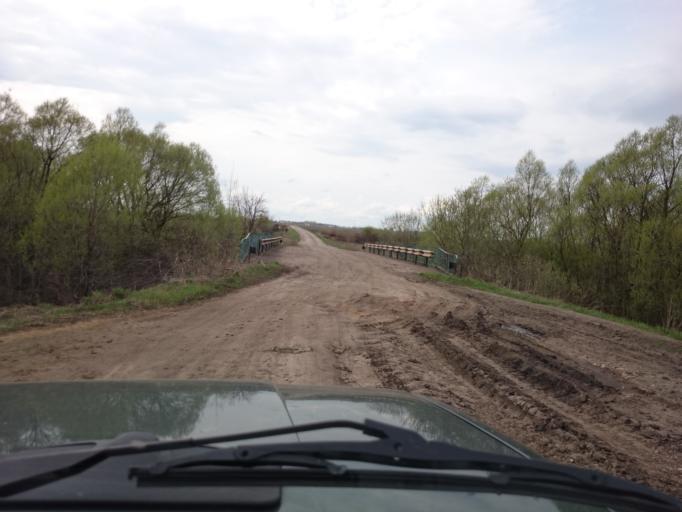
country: RU
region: Mordoviya
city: Kadoshkino
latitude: 54.0182
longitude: 44.4556
